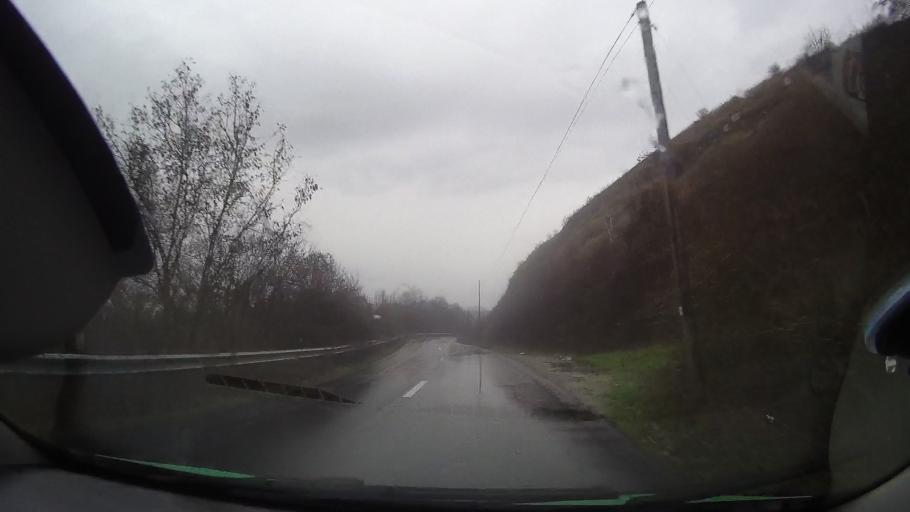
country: RO
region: Bihor
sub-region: Comuna Pocola
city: Pocola
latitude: 46.6845
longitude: 22.2599
